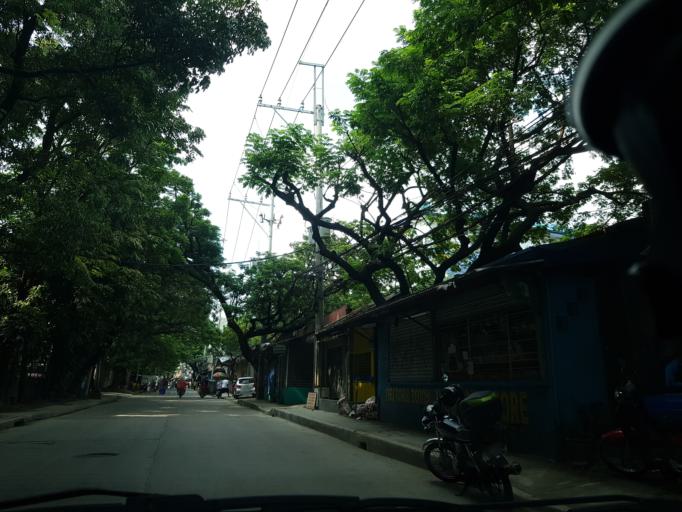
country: PH
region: Calabarzon
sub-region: Province of Rizal
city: Cainta
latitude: 14.5759
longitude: 121.0938
